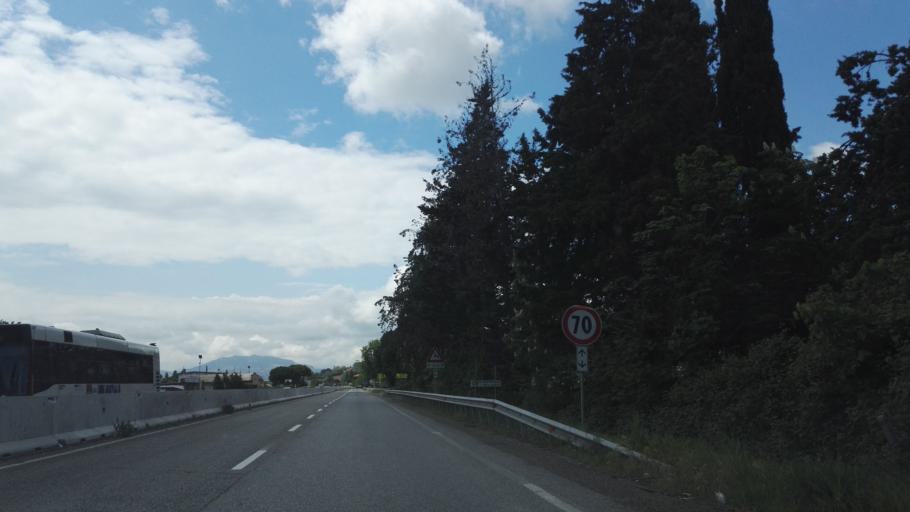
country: IT
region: Emilia-Romagna
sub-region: Provincia di Rimini
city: Rimini
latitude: 44.0350
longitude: 12.5610
